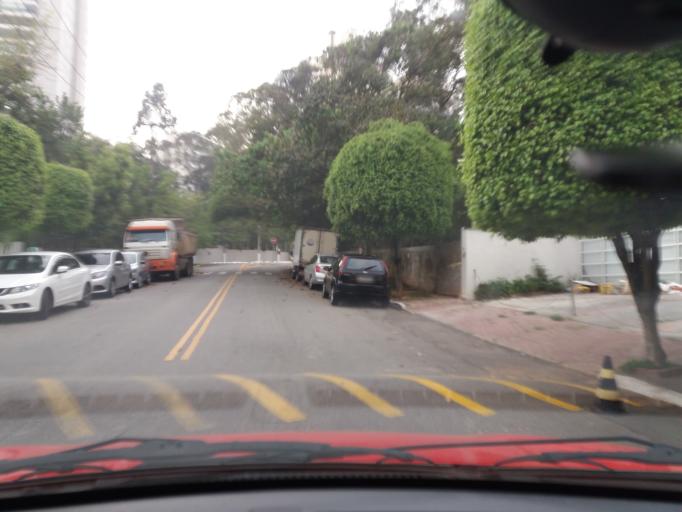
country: BR
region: Sao Paulo
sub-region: Taboao Da Serra
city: Taboao da Serra
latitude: -23.6255
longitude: -46.7413
